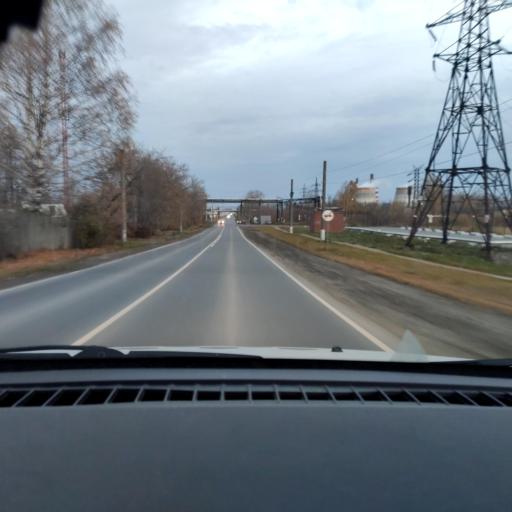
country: RU
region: Perm
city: Gamovo
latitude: 57.9118
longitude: 56.1590
